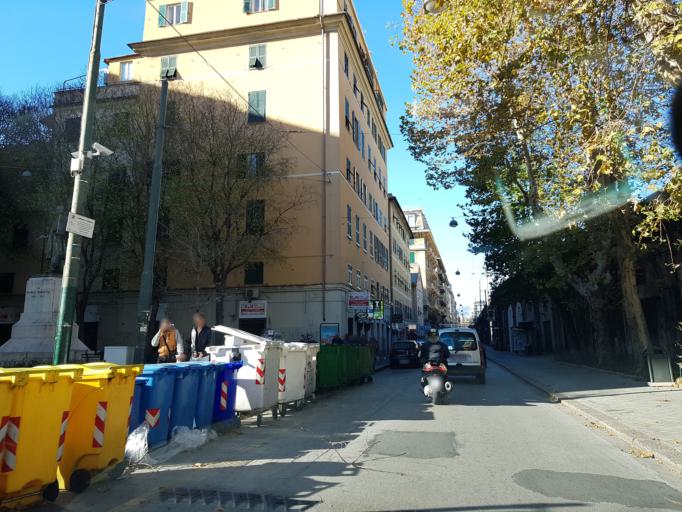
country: IT
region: Liguria
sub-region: Provincia di Genova
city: San Teodoro
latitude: 44.4088
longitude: 8.8971
